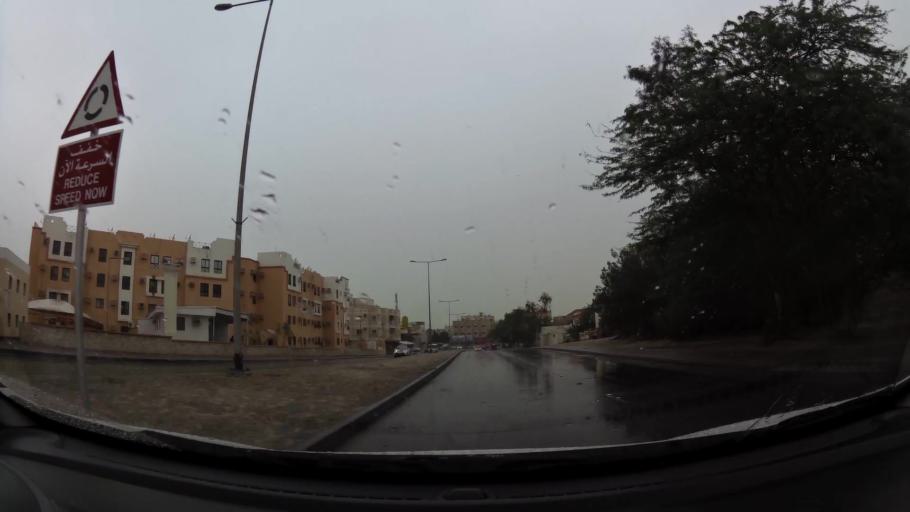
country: BH
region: Northern
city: Madinat `Isa
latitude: 26.1770
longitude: 50.5511
